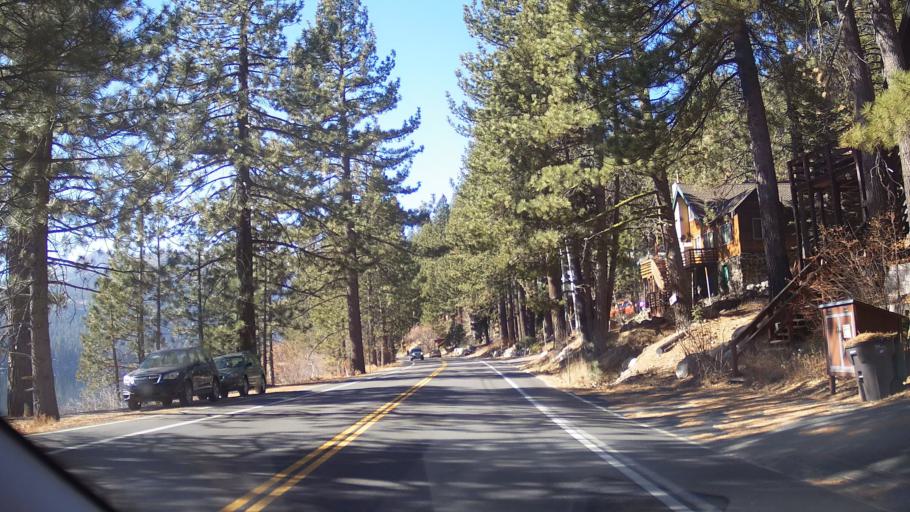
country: US
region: California
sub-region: Nevada County
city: Truckee
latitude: 39.3262
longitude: -120.2675
